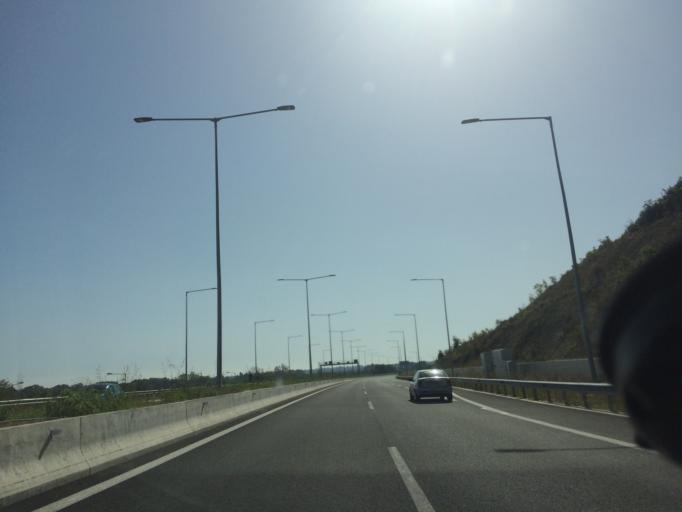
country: GR
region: Thessaly
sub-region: Nomos Larisis
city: Pyrgetos
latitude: 39.9775
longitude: 22.6313
